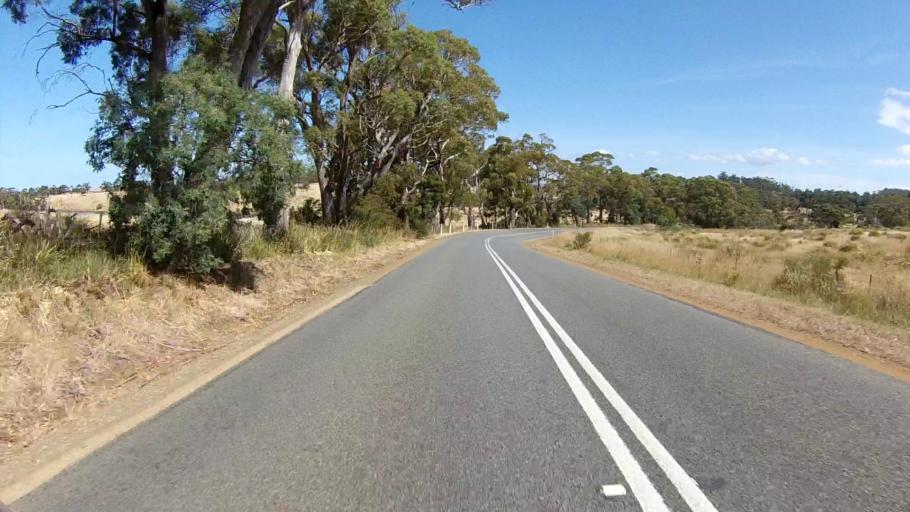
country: AU
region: Tasmania
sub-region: Sorell
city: Sorell
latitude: -42.3033
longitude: 147.9704
